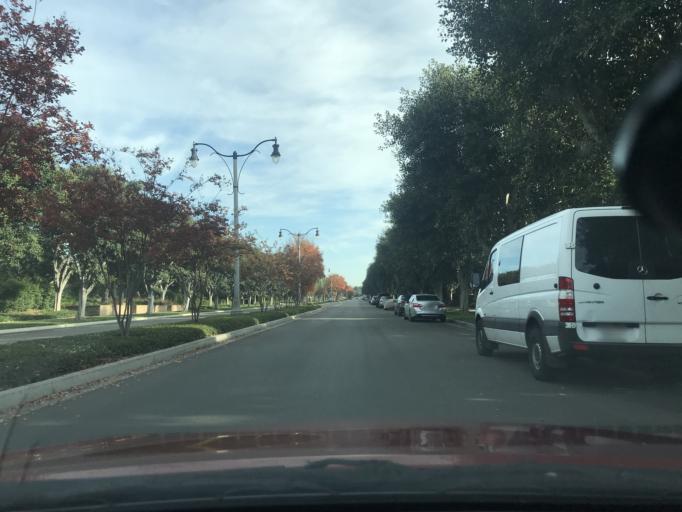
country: US
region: California
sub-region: Orange County
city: North Tustin
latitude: 33.7033
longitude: -117.7502
